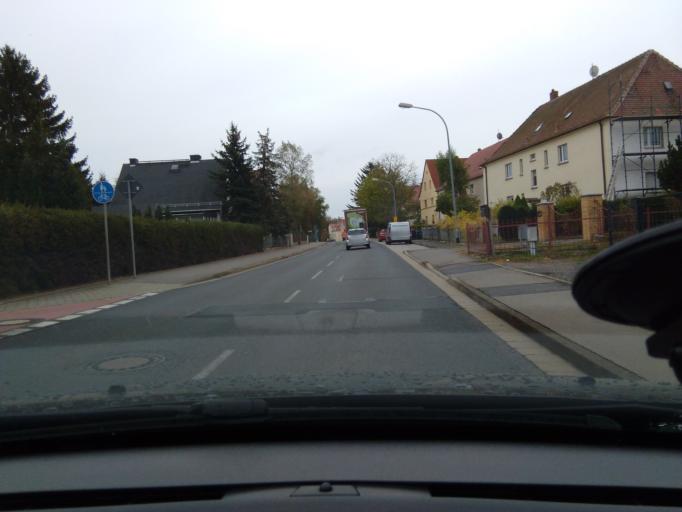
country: DE
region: Saxony
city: Niederau
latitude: 51.1485
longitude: 13.5347
